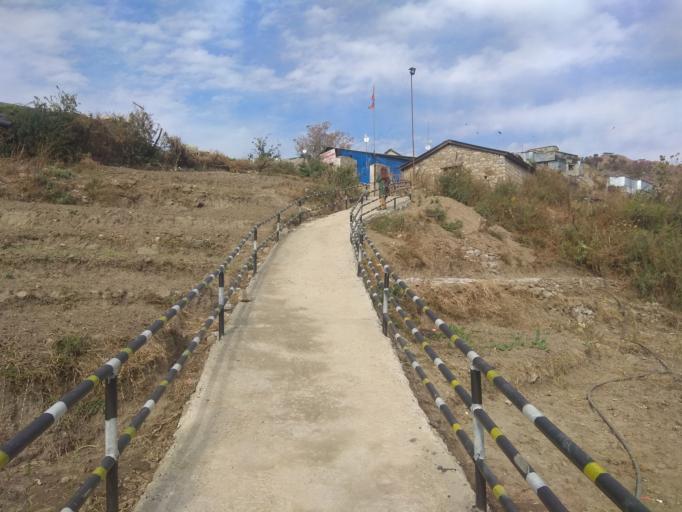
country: NP
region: Far Western
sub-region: Seti Zone
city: Achham
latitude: 29.2379
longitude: 81.6371
